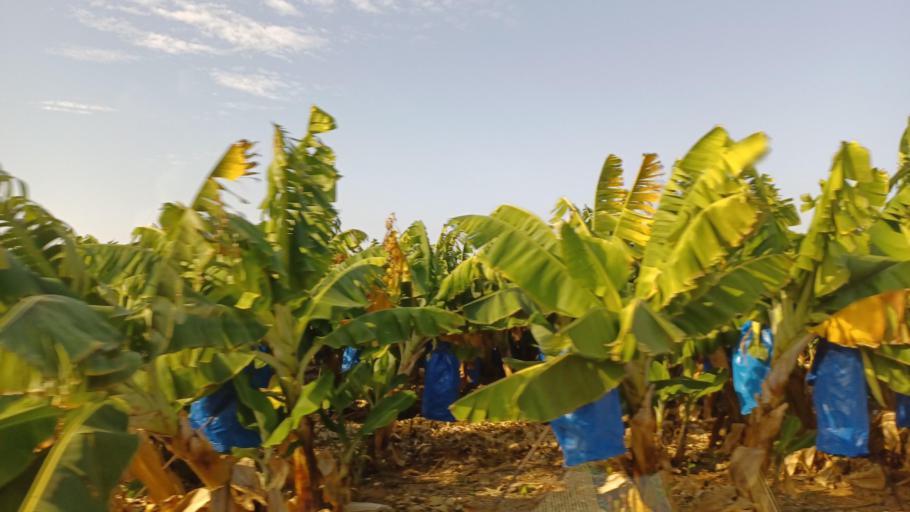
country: CY
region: Pafos
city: Pegeia
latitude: 34.8581
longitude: 32.3823
